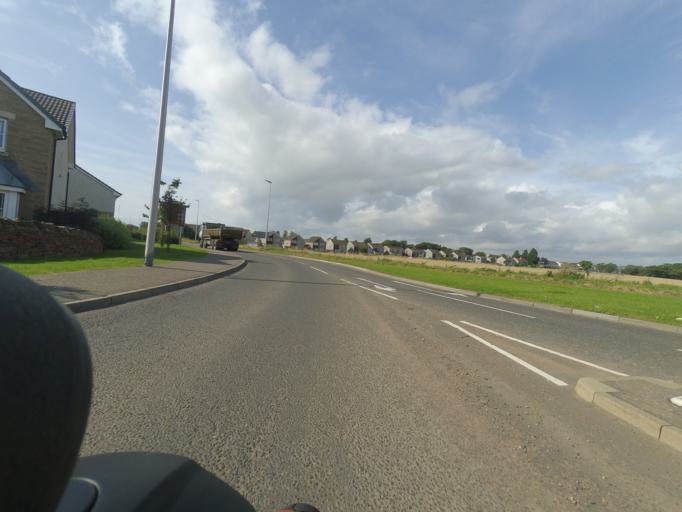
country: GB
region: Scotland
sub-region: Angus
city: Arbroath
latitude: 56.5746
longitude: -2.5749
